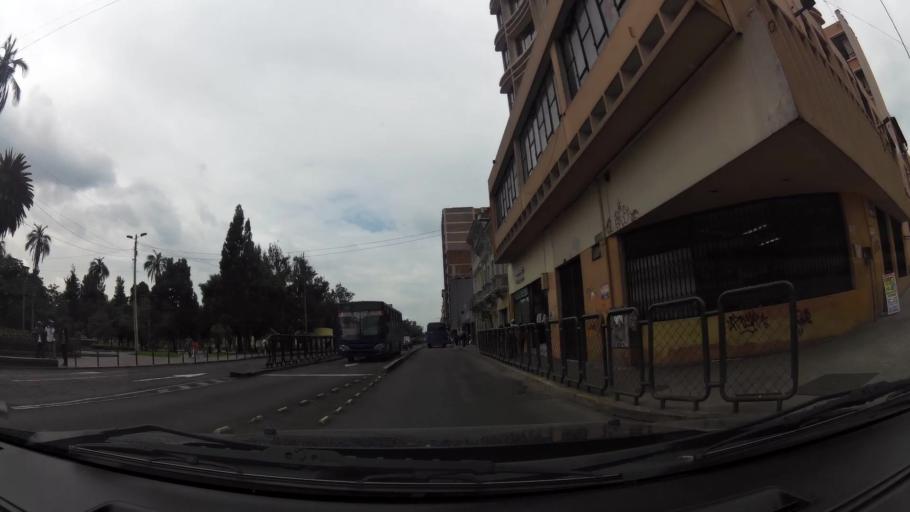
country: EC
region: Pichincha
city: Quito
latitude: -0.2163
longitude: -78.5038
